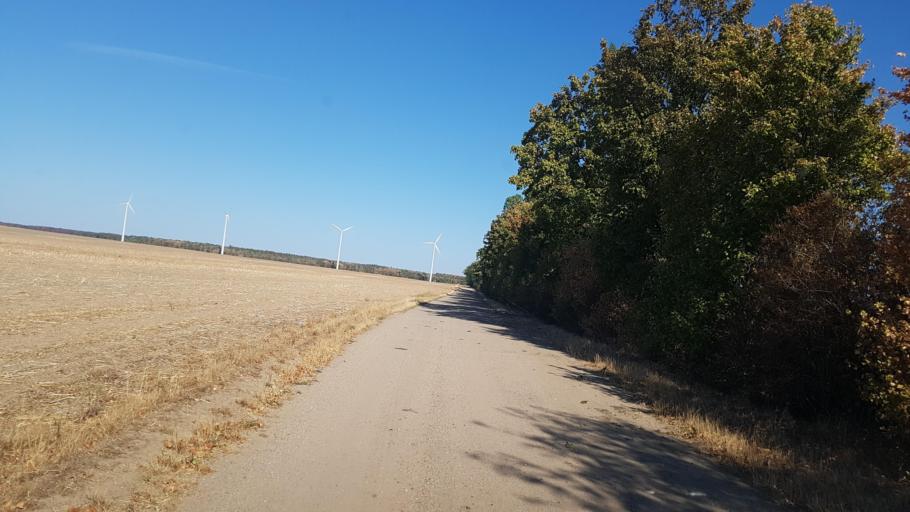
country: DE
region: Brandenburg
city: Muhlberg
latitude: 51.4056
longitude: 13.2675
